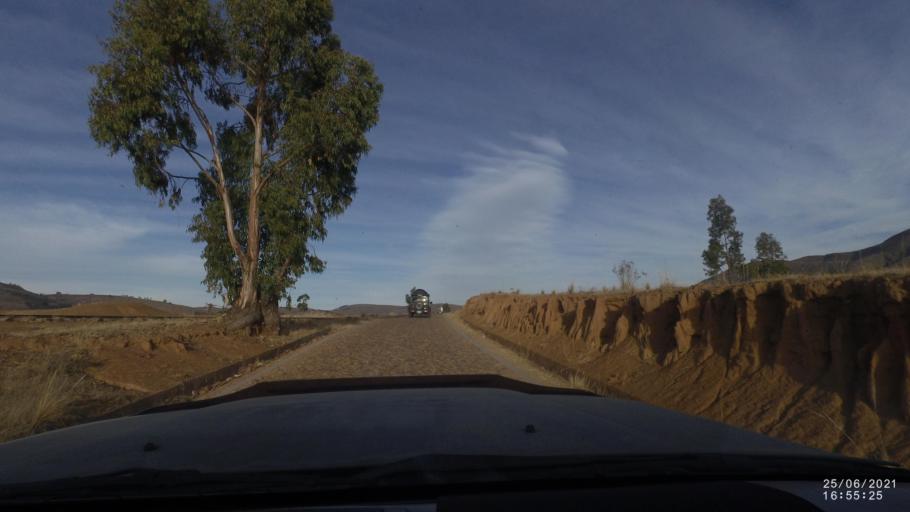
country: BO
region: Cochabamba
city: Arani
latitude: -17.8210
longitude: -65.7740
